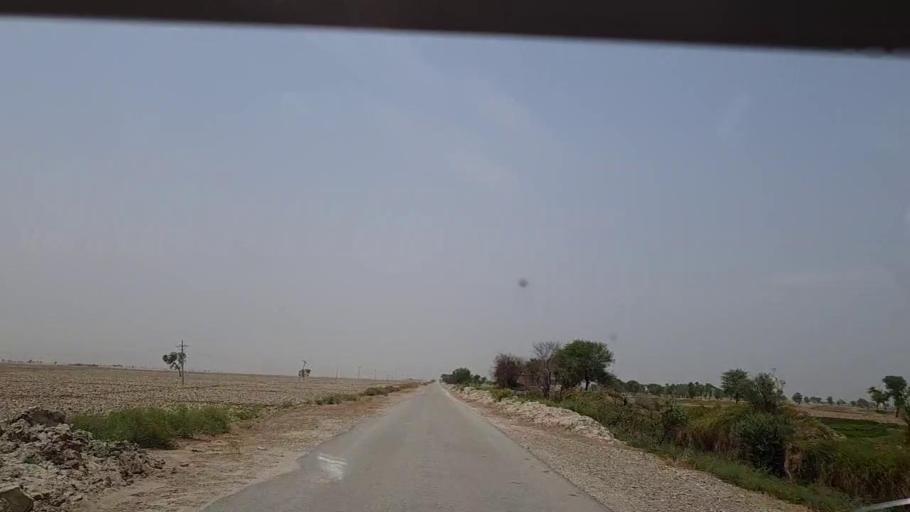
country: PK
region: Sindh
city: Khairpur Nathan Shah
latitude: 27.0240
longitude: 67.6210
